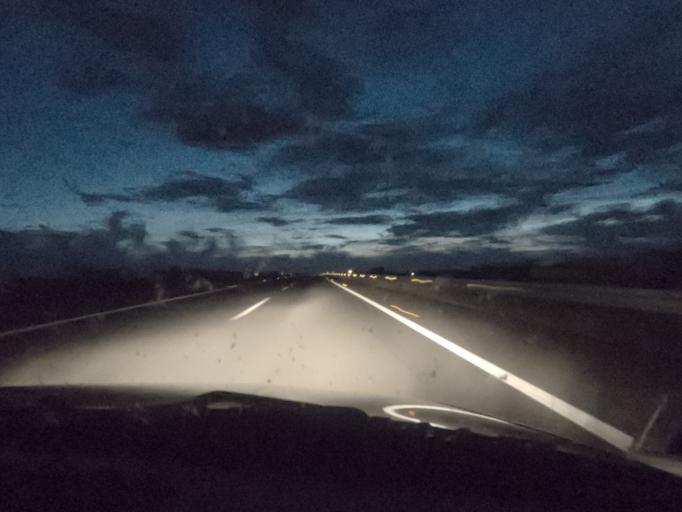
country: ES
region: Extremadura
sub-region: Provincia de Caceres
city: Morcillo
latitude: 39.9740
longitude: -6.3527
